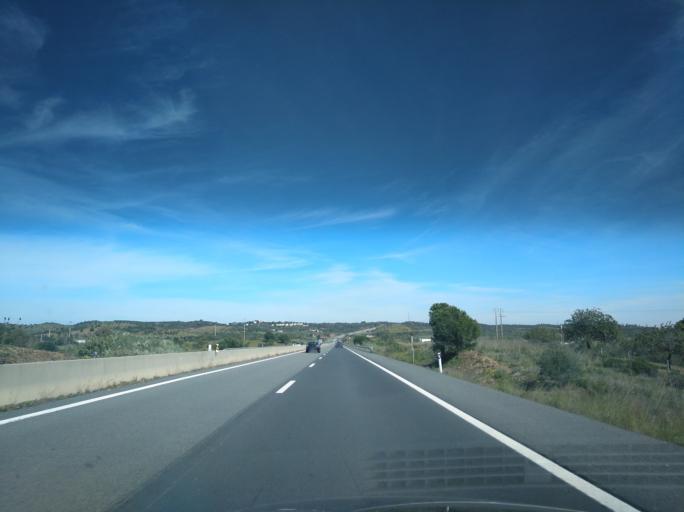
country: PT
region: Faro
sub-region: Castro Marim
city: Castro Marim
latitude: 37.2150
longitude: -7.4828
